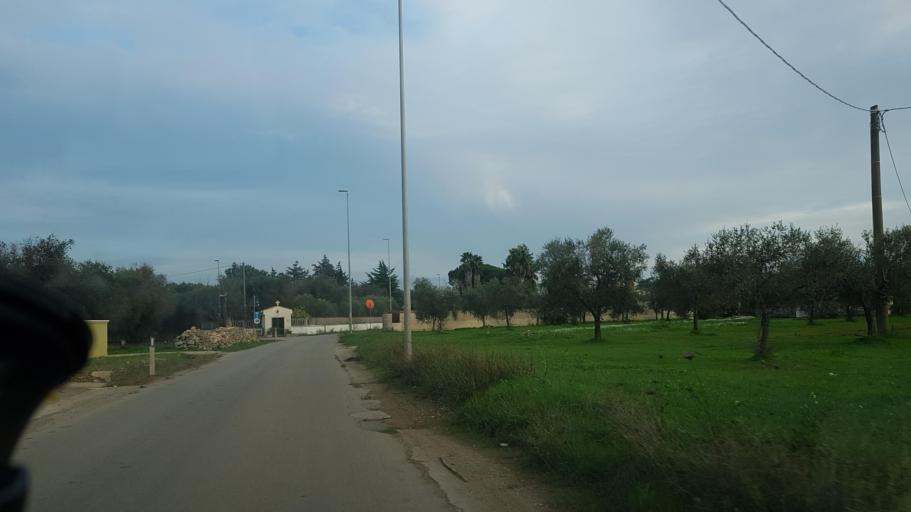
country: IT
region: Apulia
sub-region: Provincia di Brindisi
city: Latiano
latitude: 40.5455
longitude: 17.7323
